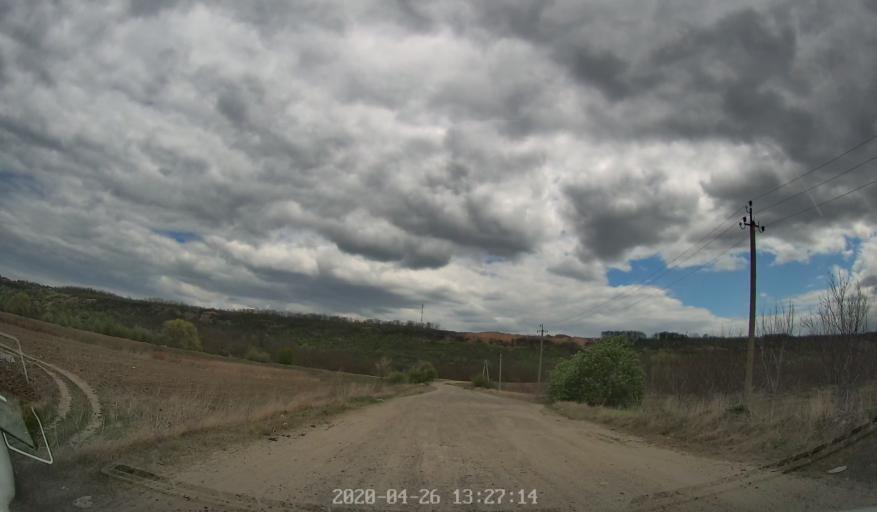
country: MD
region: Criuleni
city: Criuleni
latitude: 47.2054
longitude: 29.1751
